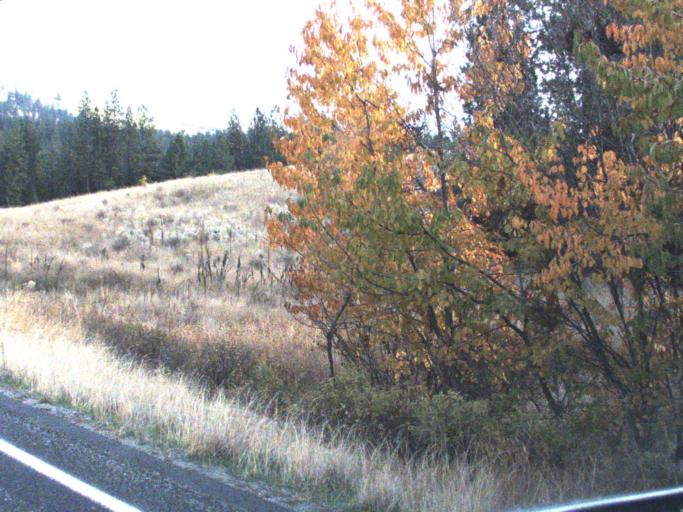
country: US
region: Washington
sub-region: Stevens County
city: Kettle Falls
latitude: 48.2011
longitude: -118.1730
